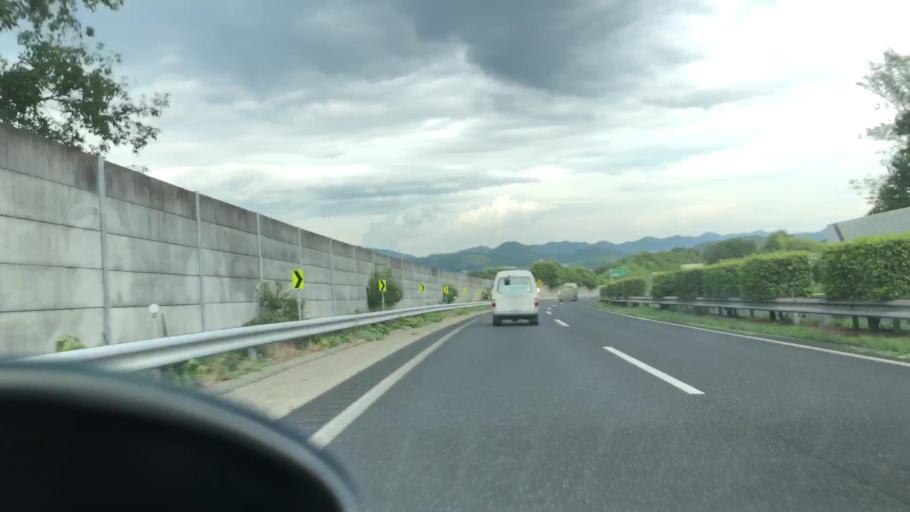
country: JP
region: Hyogo
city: Yashiro
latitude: 34.9357
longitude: 134.8504
